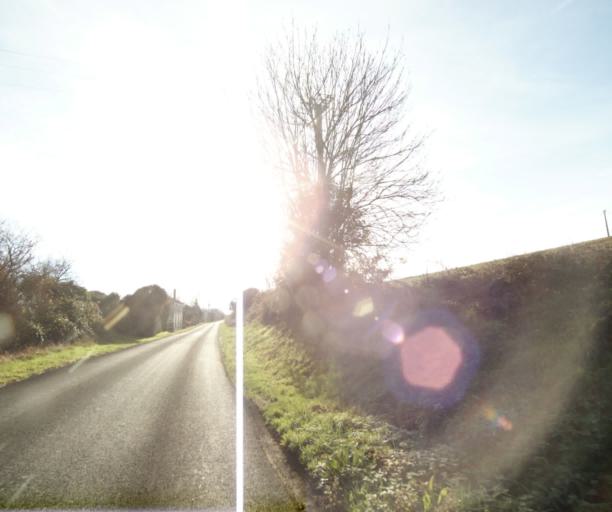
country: FR
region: Poitou-Charentes
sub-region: Departement de la Charente-Maritime
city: Chaniers
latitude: 45.7152
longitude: -0.5235
